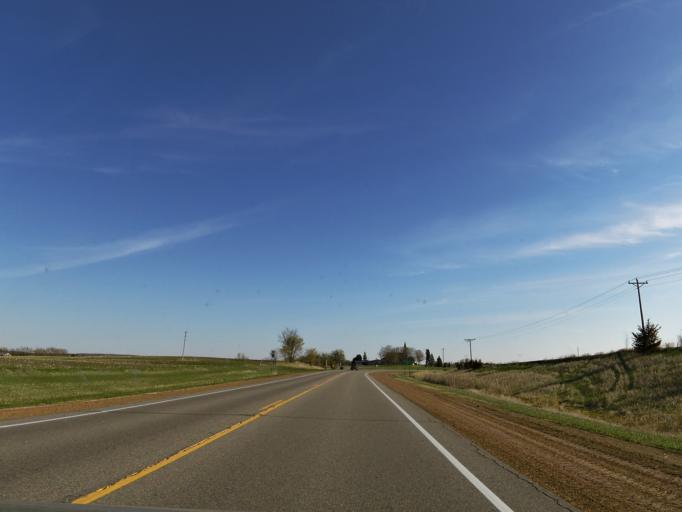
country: US
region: Minnesota
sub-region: Le Sueur County
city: New Prague
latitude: 44.5999
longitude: -93.5013
